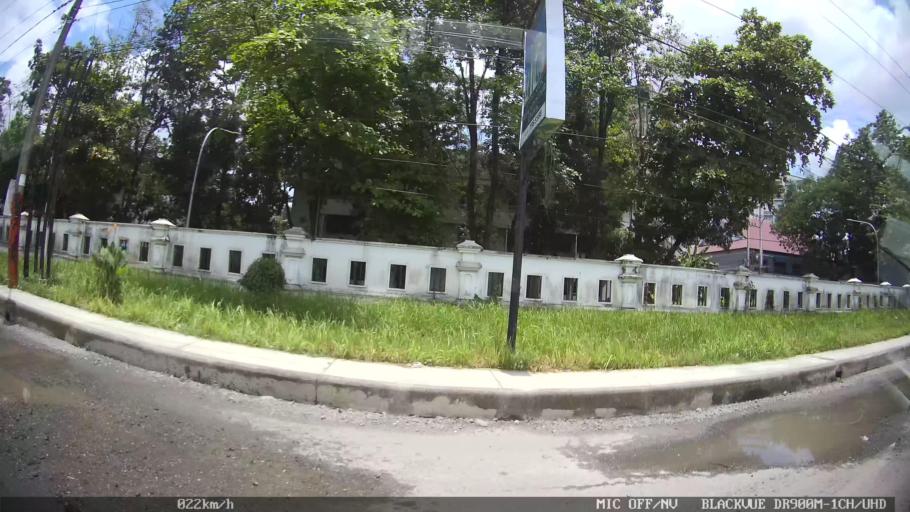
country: ID
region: North Sumatra
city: Medan
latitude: 3.6063
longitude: 98.7145
